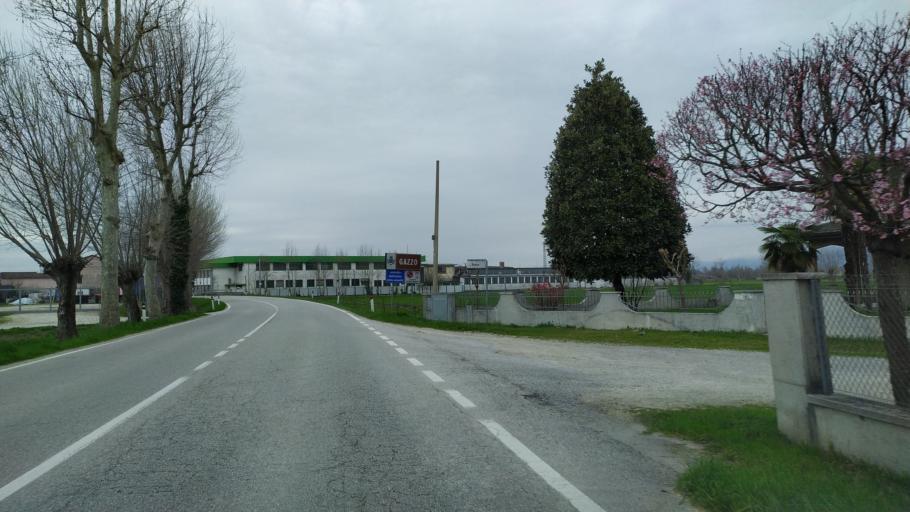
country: IT
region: Veneto
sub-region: Provincia di Padova
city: Gazzo
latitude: 45.5836
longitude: 11.7212
